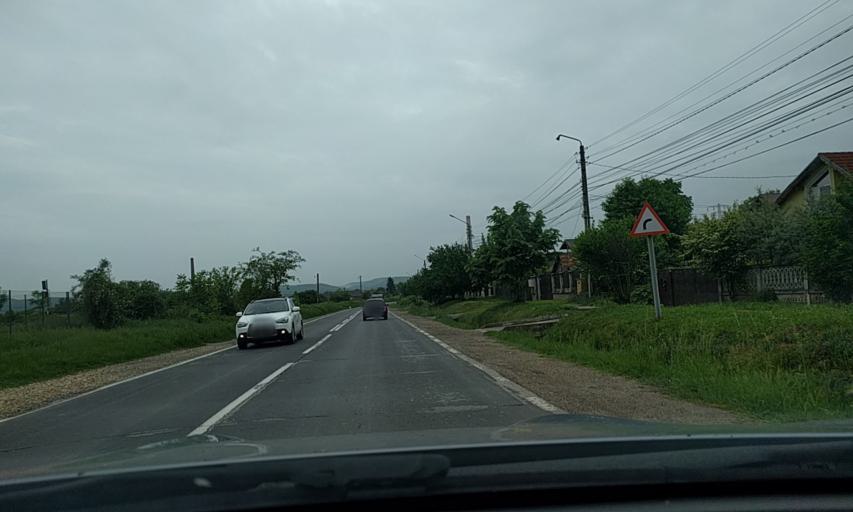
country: RO
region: Dambovita
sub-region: Comuna Doicesti
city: Doicesti
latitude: 44.9891
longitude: 25.4103
